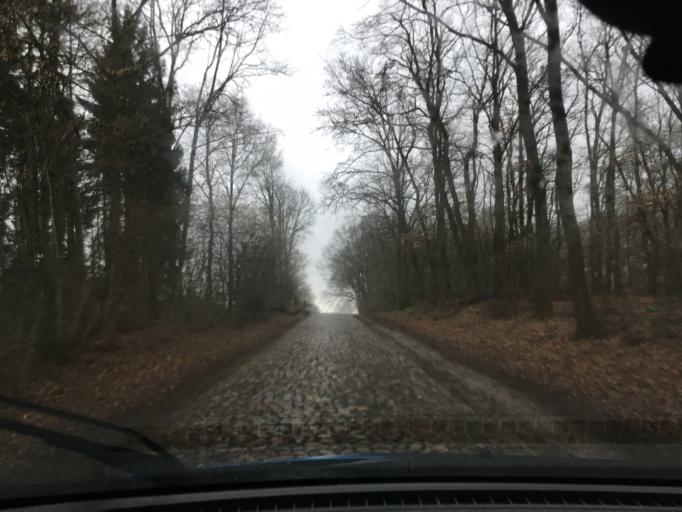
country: DE
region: Schleswig-Holstein
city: Kruzen
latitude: 53.4150
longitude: 10.5281
